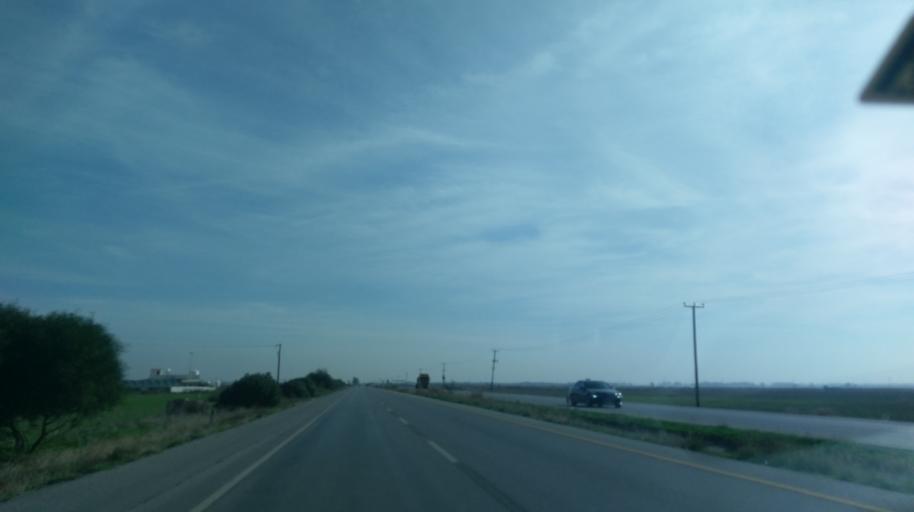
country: CY
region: Larnaka
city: Athienou
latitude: 35.2118
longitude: 33.5360
